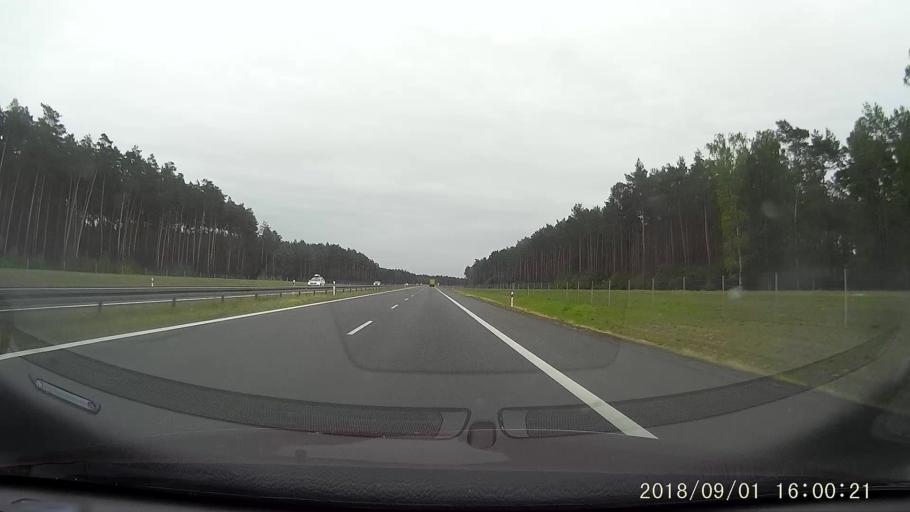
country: PL
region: Lubusz
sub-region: Powiat gorzowski
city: Deszczno
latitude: 52.6436
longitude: 15.3540
